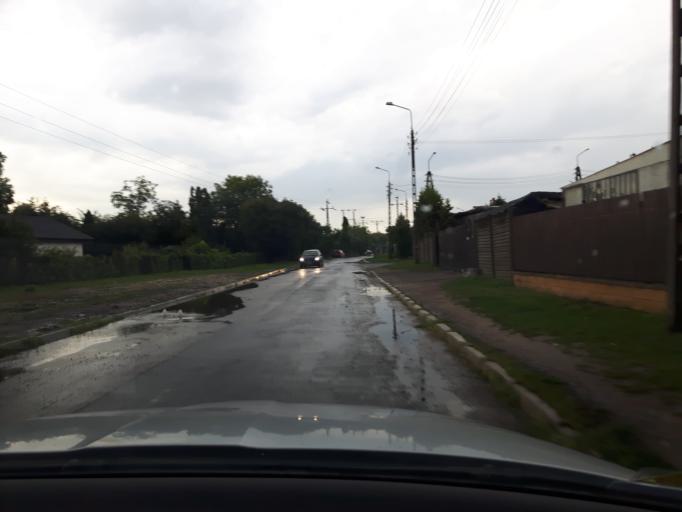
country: PL
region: Masovian Voivodeship
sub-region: Powiat wolominski
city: Zabki
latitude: 52.2914
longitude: 21.0994
